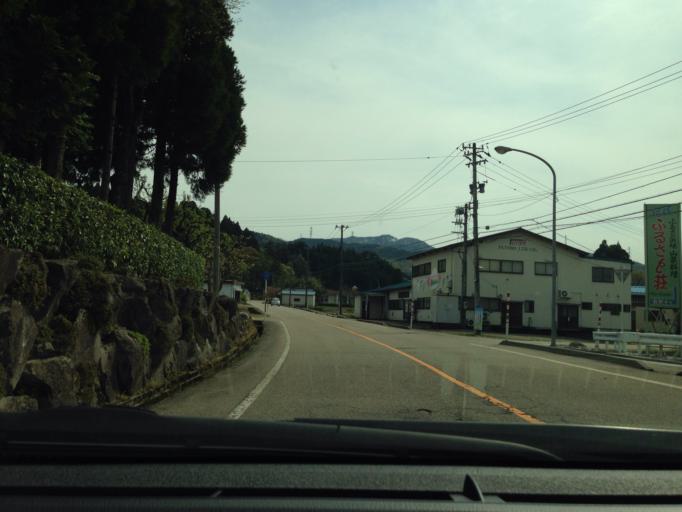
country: JP
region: Toyama
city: Fukumitsu
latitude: 36.5069
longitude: 136.8481
